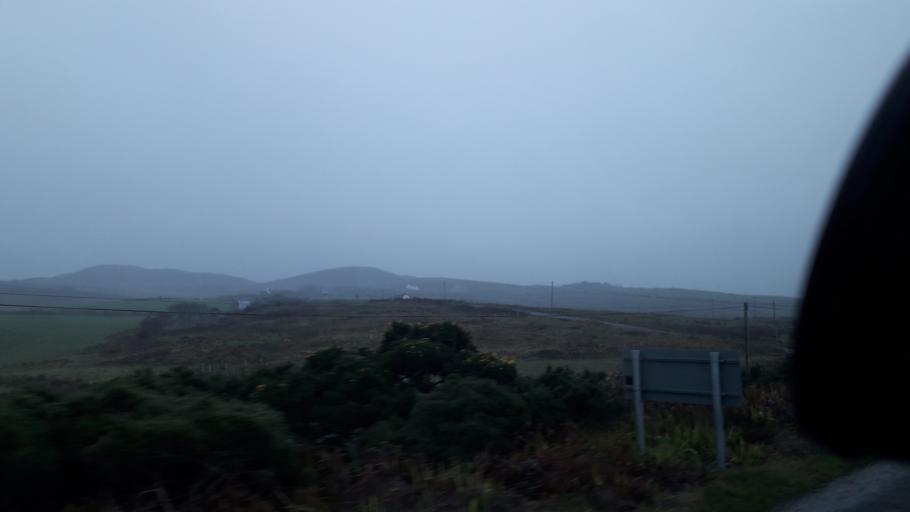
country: IE
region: Ulster
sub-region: County Donegal
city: Buncrana
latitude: 55.2762
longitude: -7.6376
